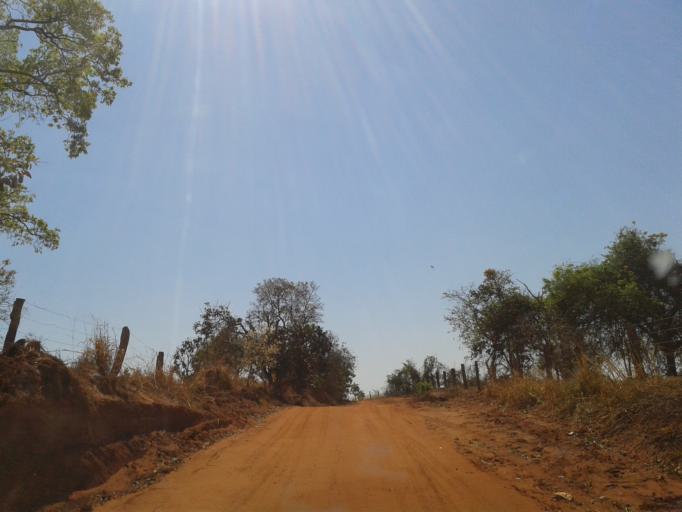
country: BR
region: Minas Gerais
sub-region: Ituiutaba
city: Ituiutaba
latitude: -19.0827
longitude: -49.3045
